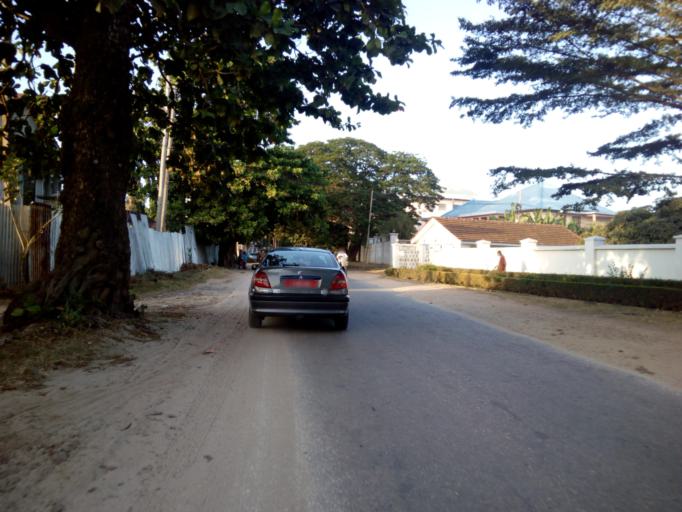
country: TZ
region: Zanzibar Urban/West
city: Zanzibar
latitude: -6.2043
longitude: 39.2100
